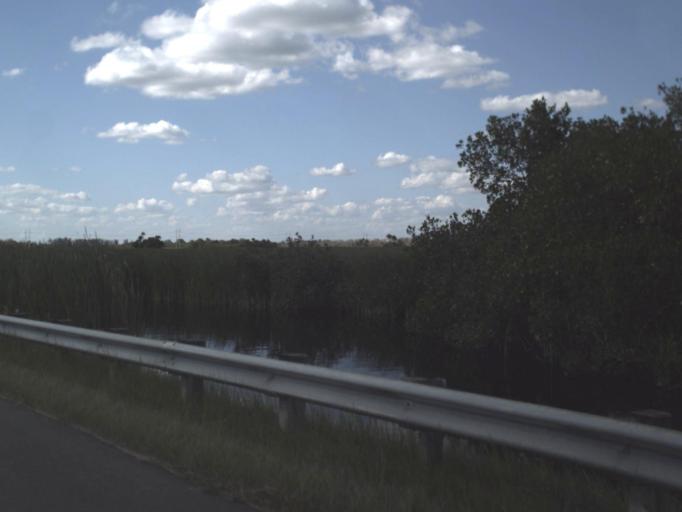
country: US
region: Florida
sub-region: Collier County
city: Marco
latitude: 25.9066
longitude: -81.3524
